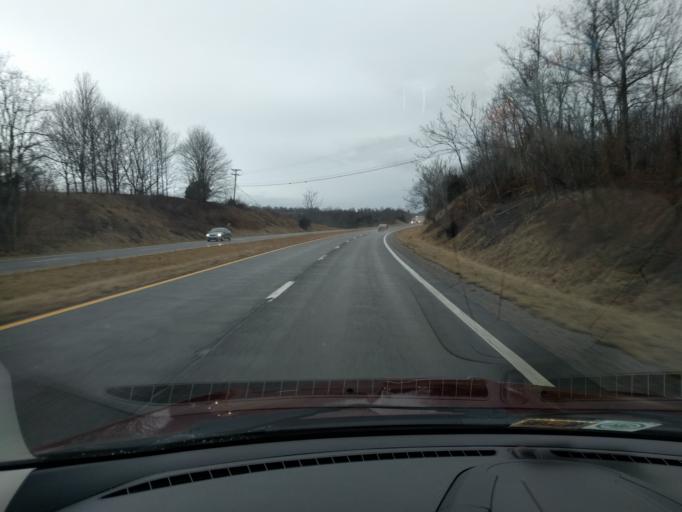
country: US
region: Virginia
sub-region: Giles County
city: Pembroke
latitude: 37.3023
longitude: -80.5691
